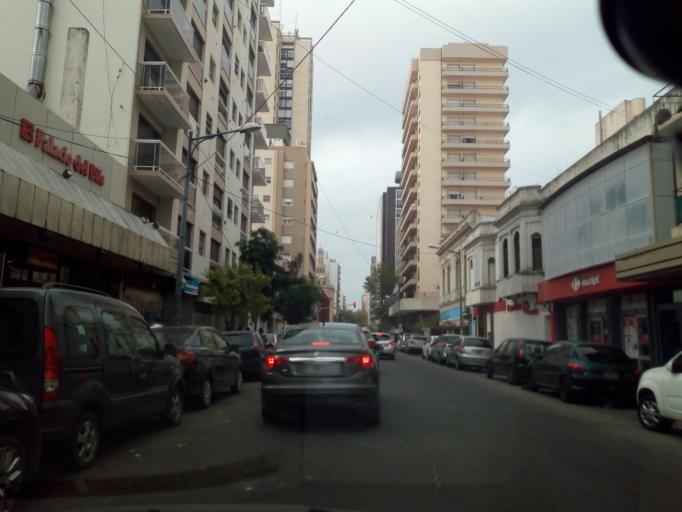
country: AR
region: Buenos Aires
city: Mar del Plata
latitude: -38.0008
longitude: -57.5480
